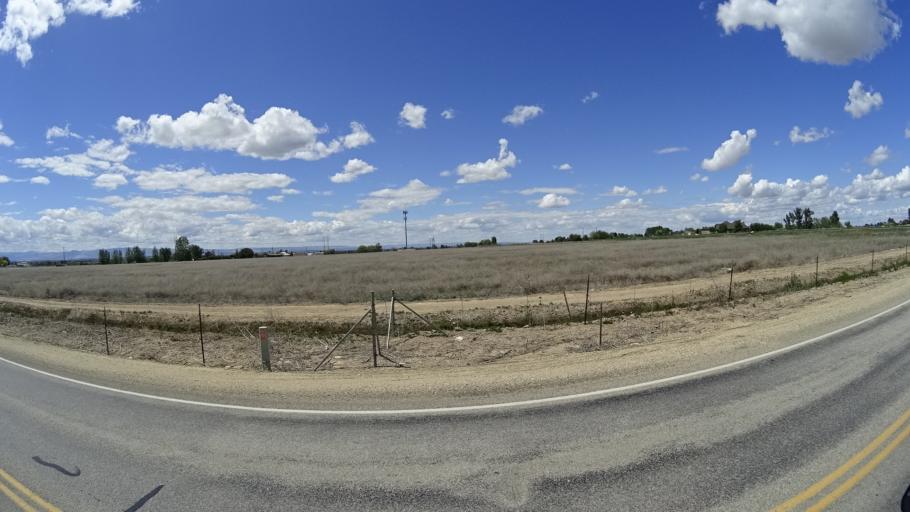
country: US
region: Idaho
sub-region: Ada County
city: Meridian
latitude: 43.5627
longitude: -116.4338
